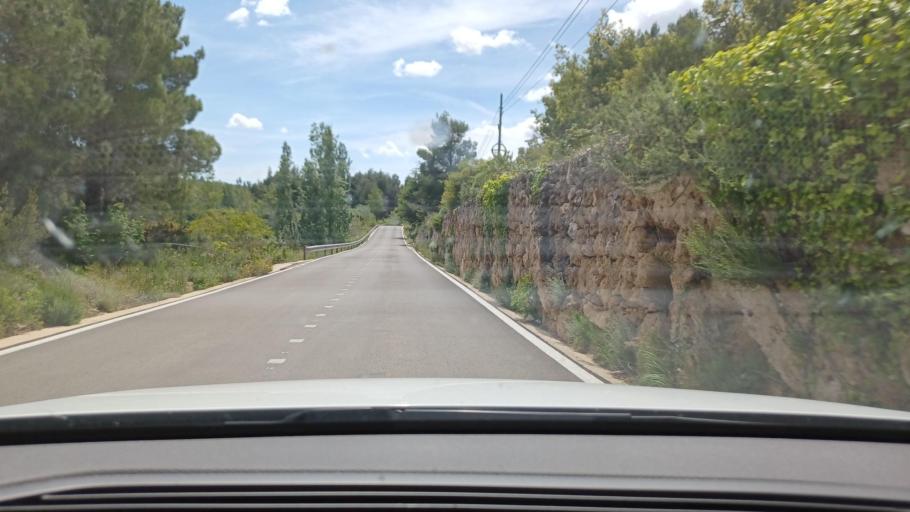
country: ES
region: Valencia
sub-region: Provincia de Castello
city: Rosell
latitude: 40.6574
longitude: 0.2673
